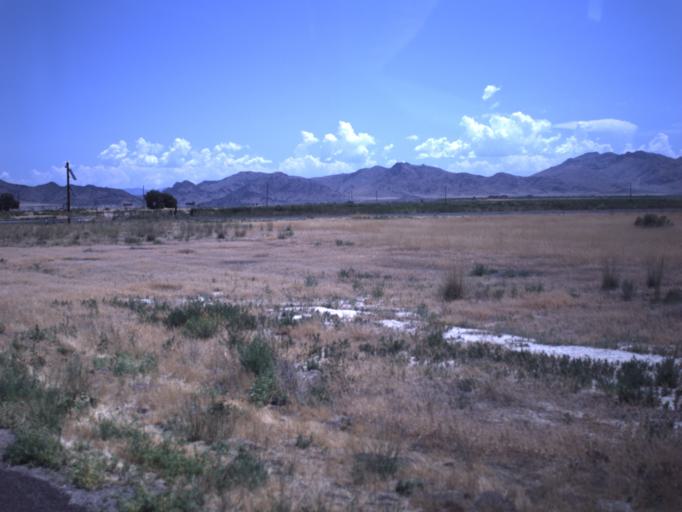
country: US
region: Utah
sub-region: Millard County
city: Delta
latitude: 39.5240
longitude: -112.3734
